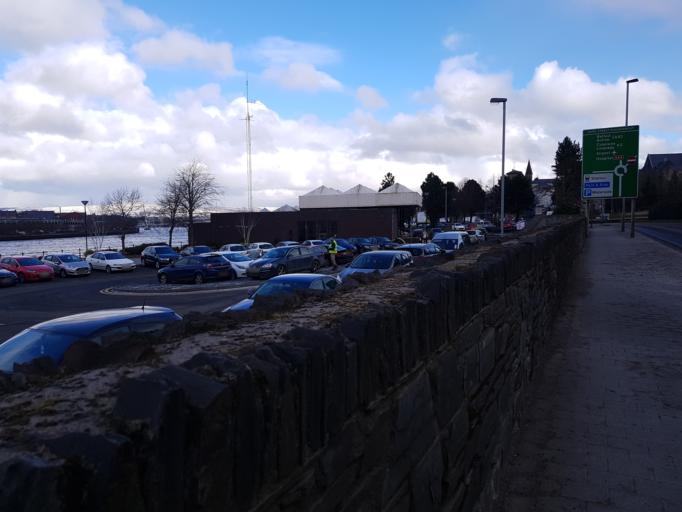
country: GB
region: Northern Ireland
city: Londonderry County Borough
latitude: 54.9913
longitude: -7.3138
